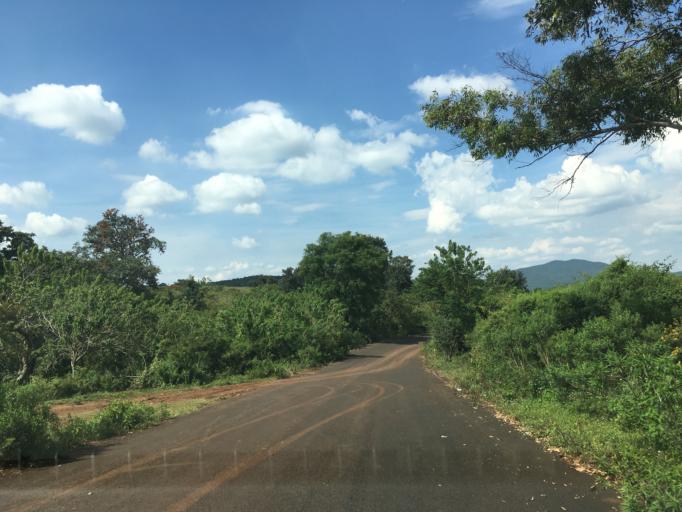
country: MX
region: Mexico
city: El Guayabito
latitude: 19.8802
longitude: -102.5007
